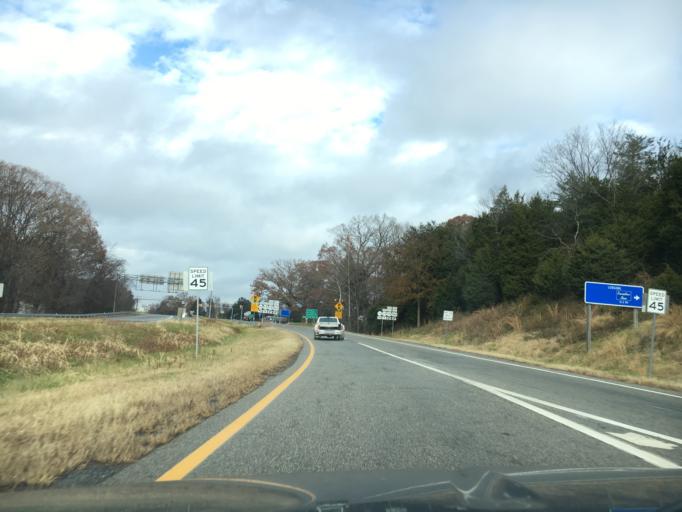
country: US
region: Virginia
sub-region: Prince Edward County
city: Farmville
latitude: 37.3139
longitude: -78.4603
